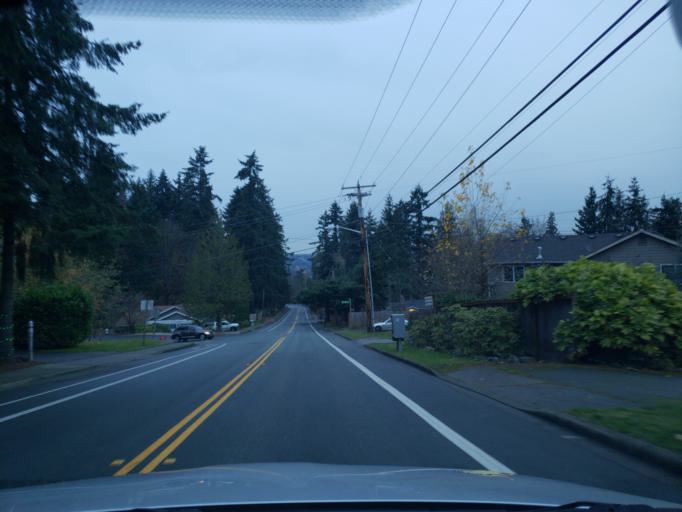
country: US
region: Washington
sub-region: King County
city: Kenmore
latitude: 47.7475
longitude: -122.2312
